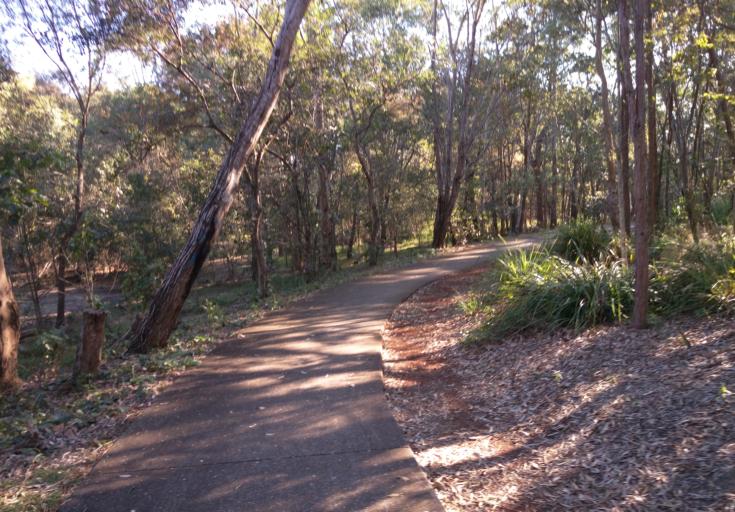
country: AU
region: Queensland
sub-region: Brisbane
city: Chandler
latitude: -27.5249
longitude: 153.1986
